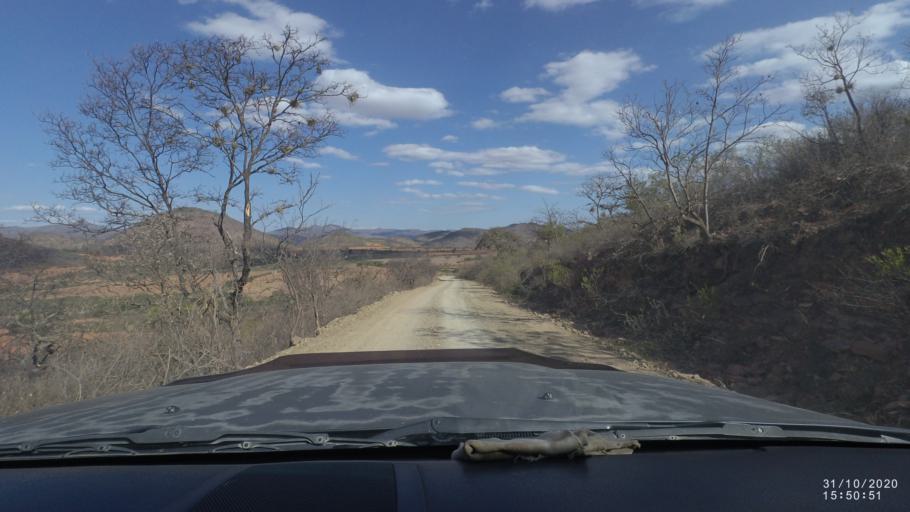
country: BO
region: Chuquisaca
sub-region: Provincia Zudanez
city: Mojocoya
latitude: -18.3135
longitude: -64.7043
